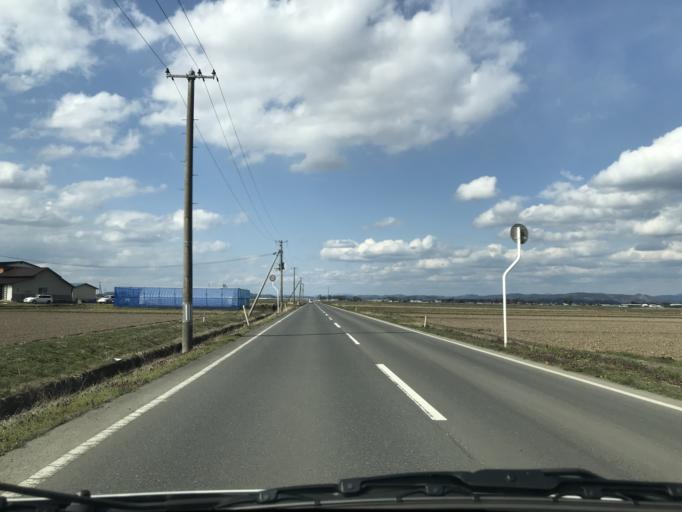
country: JP
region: Miyagi
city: Wakuya
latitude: 38.6631
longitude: 141.2302
